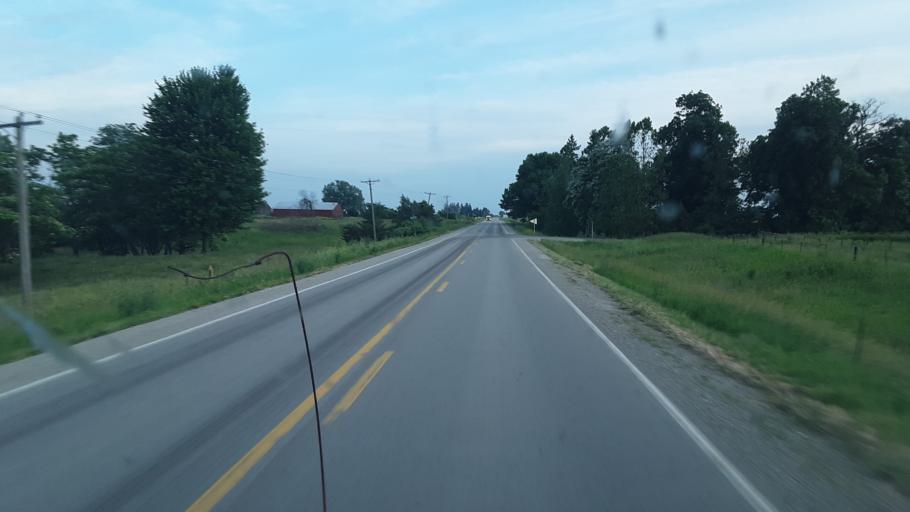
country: US
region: Iowa
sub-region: Iowa County
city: Marengo
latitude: 41.7184
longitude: -92.1827
